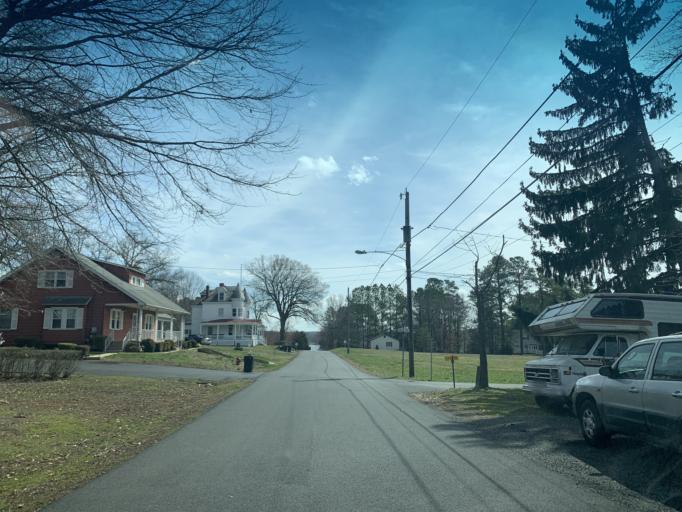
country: US
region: Maryland
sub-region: Cecil County
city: Charlestown
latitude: 39.5753
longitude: -75.9738
